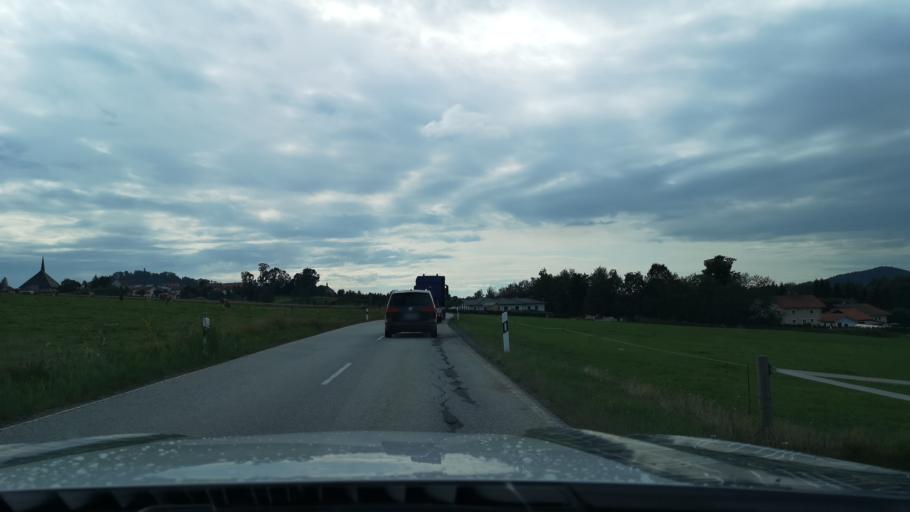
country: DE
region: Bavaria
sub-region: Lower Bavaria
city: Jandelsbrunn
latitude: 48.7333
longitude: 13.7023
